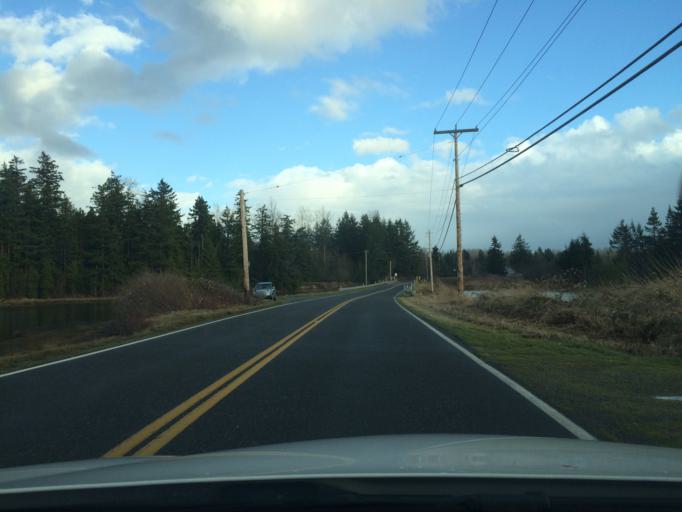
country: US
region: Washington
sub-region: Whatcom County
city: Blaine
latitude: 48.9617
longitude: -122.7352
